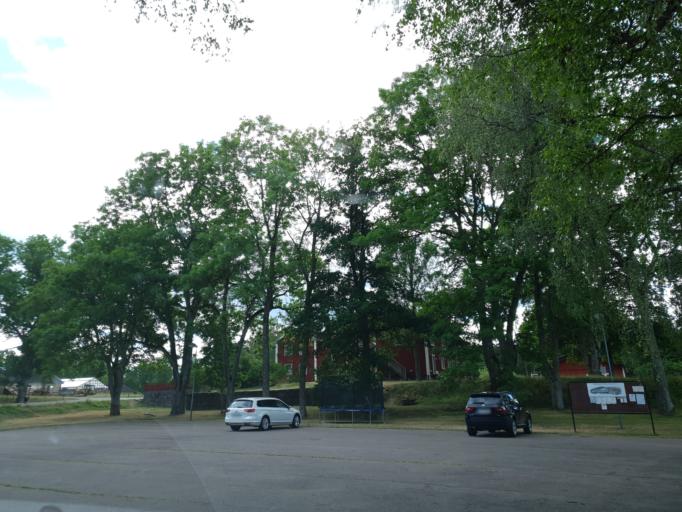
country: SE
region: Kalmar
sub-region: Emmaboda Kommun
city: Emmaboda
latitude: 56.6224
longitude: 15.6717
